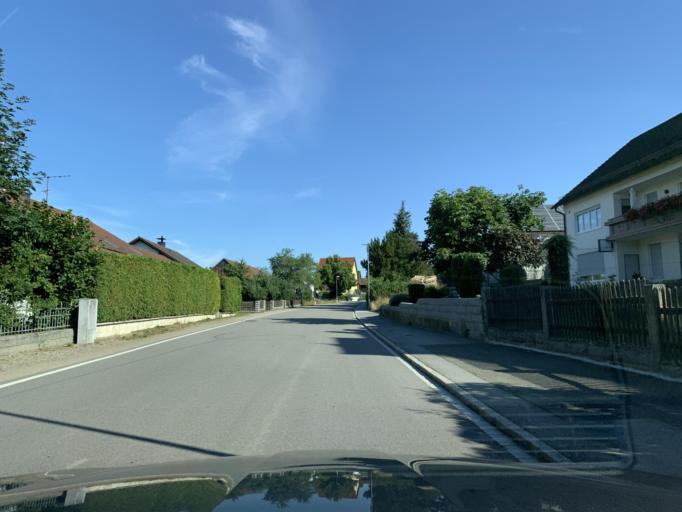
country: DE
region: Bavaria
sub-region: Upper Palatinate
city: Schwarzhofen
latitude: 49.3740
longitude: 12.3465
